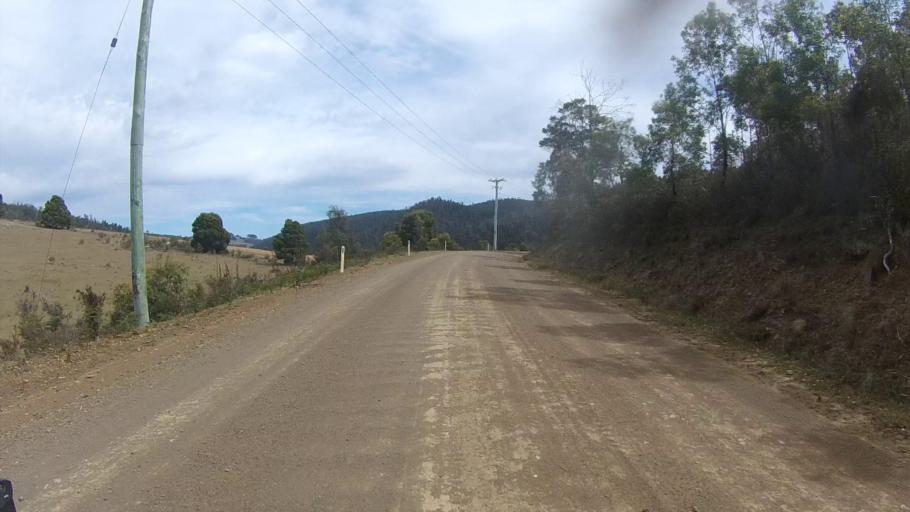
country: AU
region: Tasmania
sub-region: Sorell
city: Sorell
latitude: -42.7572
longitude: 147.8001
